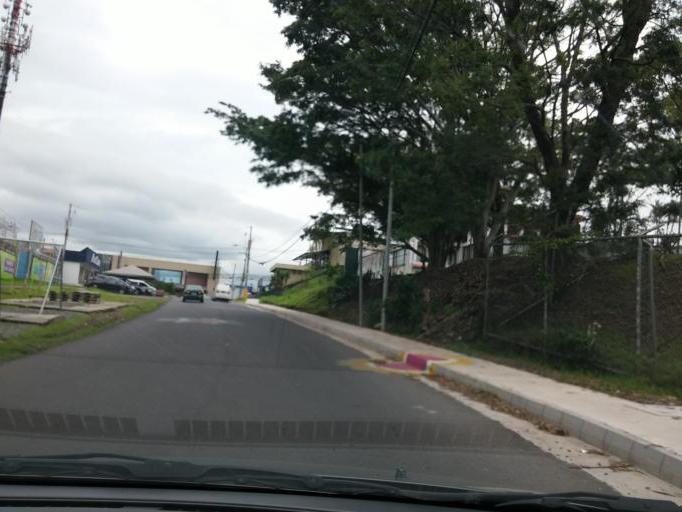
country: CR
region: San Jose
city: San Pedro
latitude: 9.9285
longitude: -84.0440
